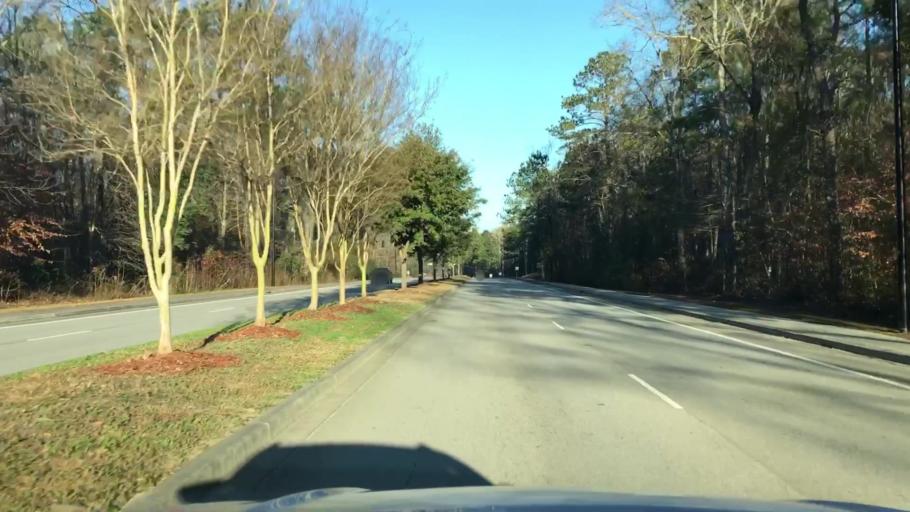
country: US
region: South Carolina
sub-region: Berkeley County
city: Ladson
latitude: 32.9245
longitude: -80.1130
